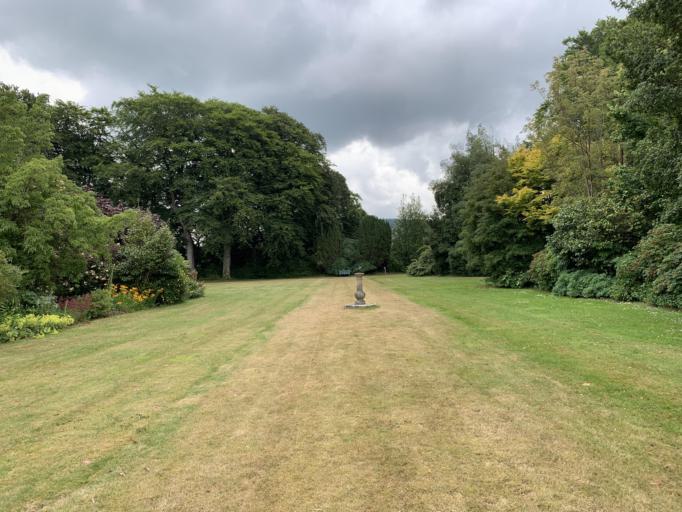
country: GB
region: Scotland
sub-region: Dumfries and Galloway
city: Stranraer
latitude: 54.9148
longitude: -4.9545
